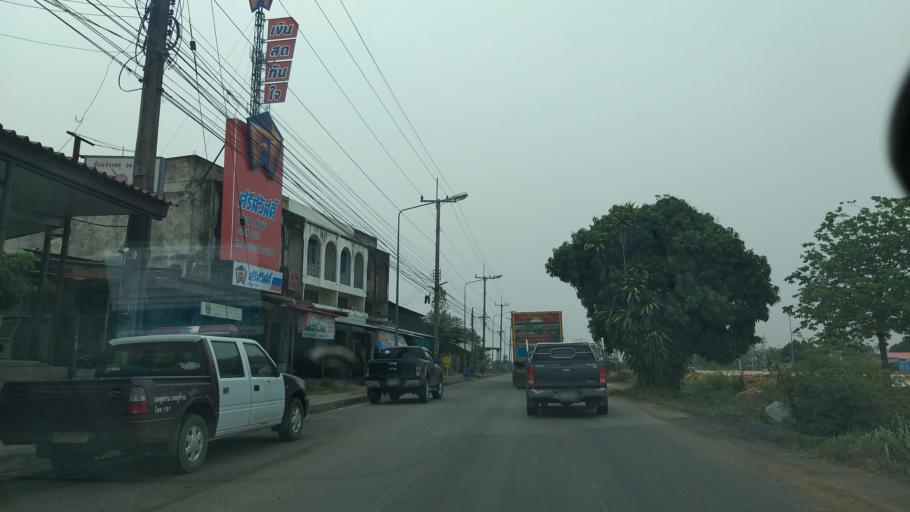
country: TH
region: Chon Buri
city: Ko Chan
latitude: 13.4857
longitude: 101.2780
